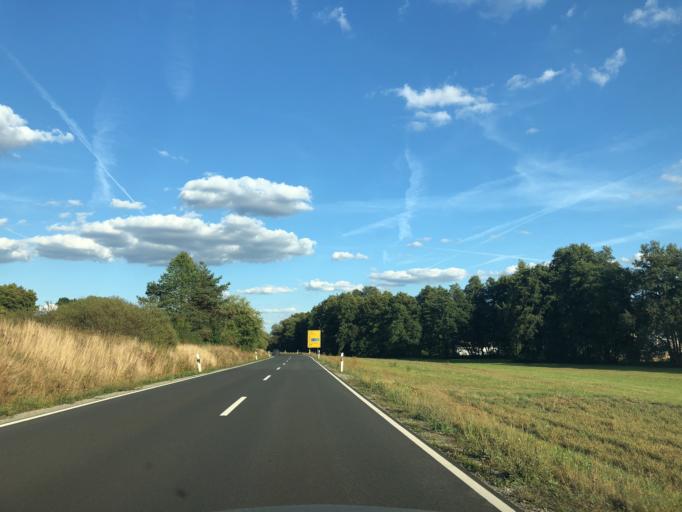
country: DE
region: Bavaria
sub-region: Upper Franconia
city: Burgwindheim
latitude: 49.8317
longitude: 10.5639
